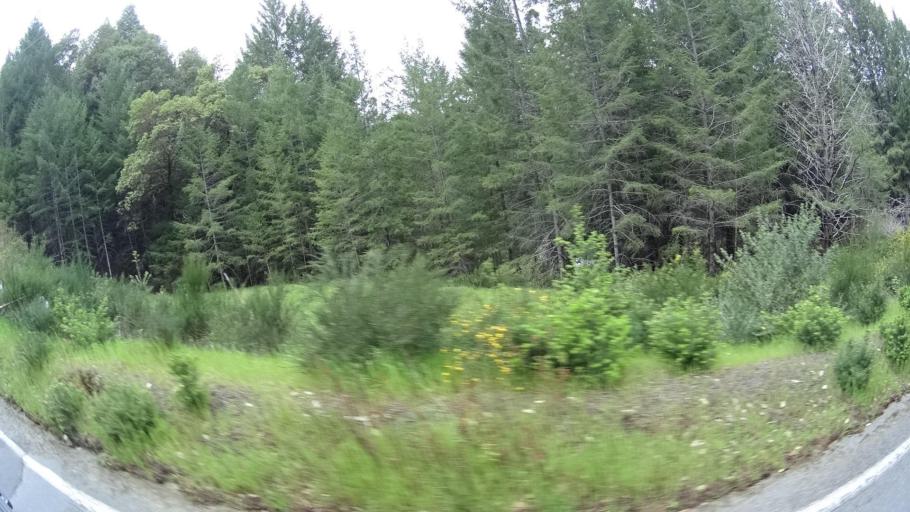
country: US
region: California
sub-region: Humboldt County
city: Redway
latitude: 40.0556
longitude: -123.9774
